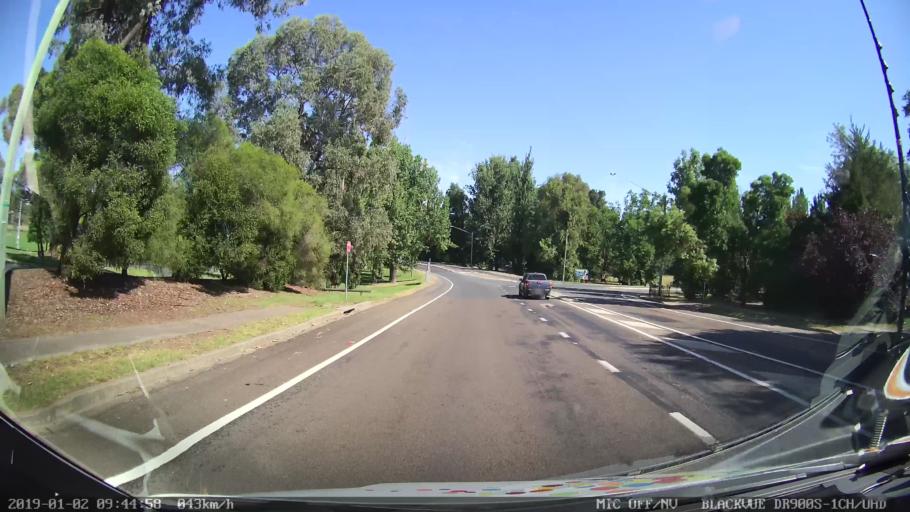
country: AU
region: New South Wales
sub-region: Tumut Shire
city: Tumut
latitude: -35.2971
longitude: 148.2226
